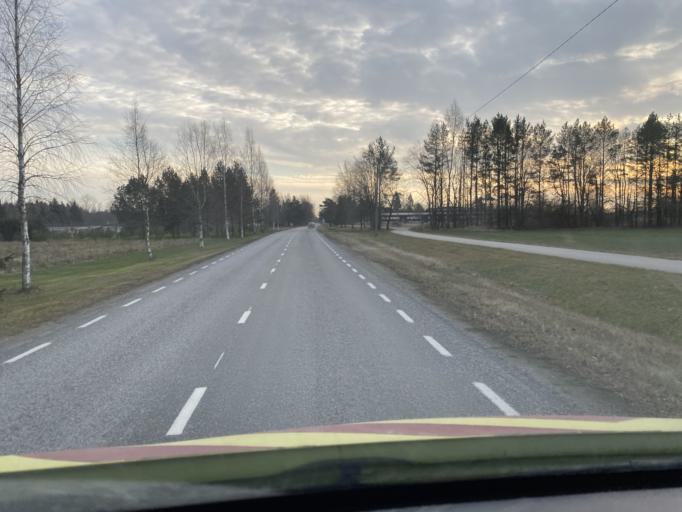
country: EE
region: Jogevamaa
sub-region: Poltsamaa linn
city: Poltsamaa
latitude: 58.6356
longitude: 25.9788
